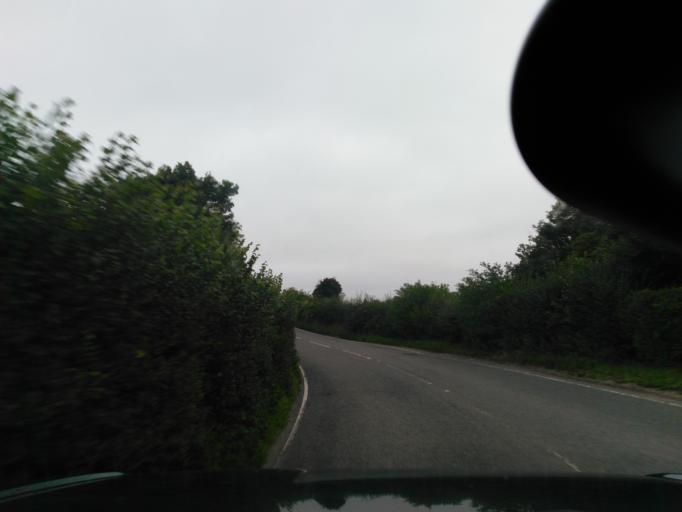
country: GB
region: England
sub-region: Dorset
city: Blandford Forum
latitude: 50.8935
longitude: -2.1934
